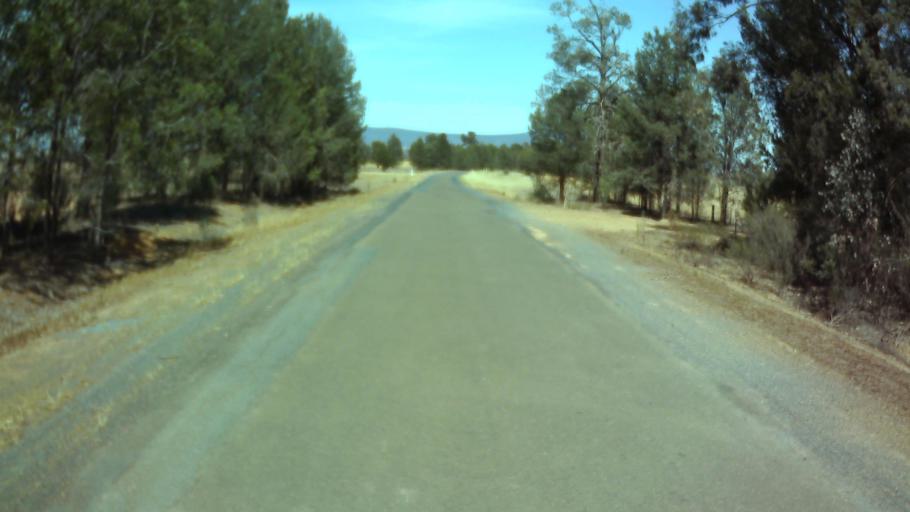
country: AU
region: New South Wales
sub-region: Weddin
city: Grenfell
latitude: -33.8705
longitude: 148.1055
